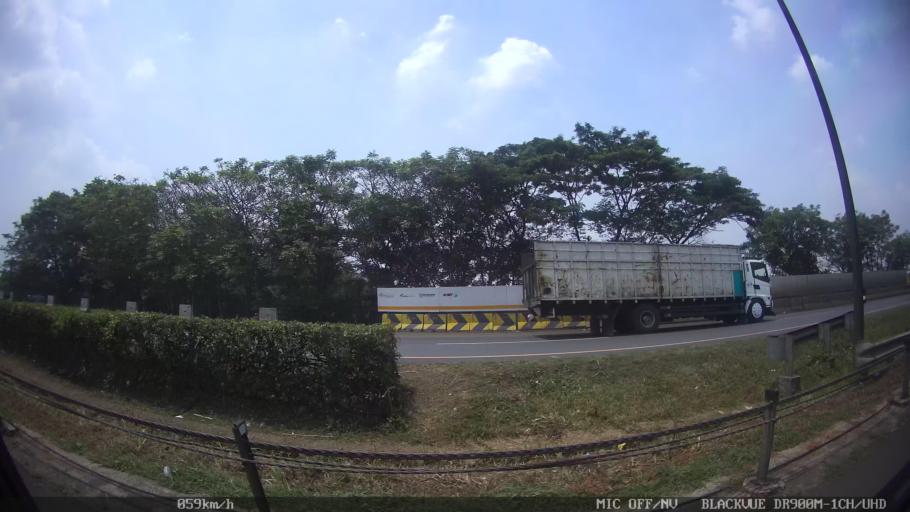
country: ID
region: Banten
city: Serang
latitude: -6.1335
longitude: 106.2078
